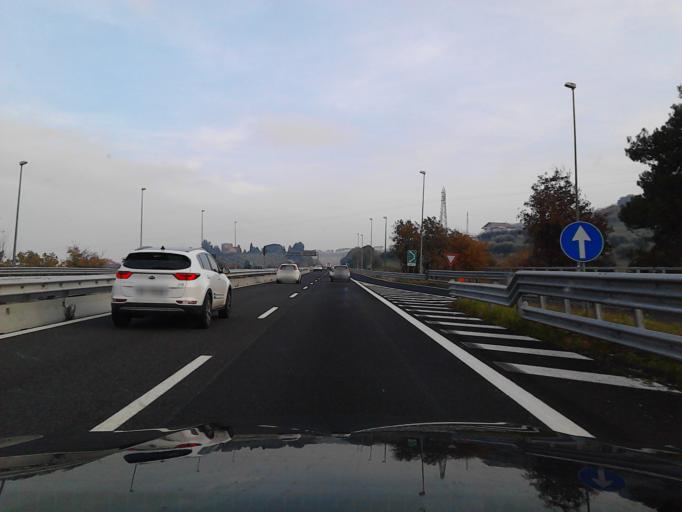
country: IT
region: Abruzzo
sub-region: Provincia di Teramo
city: Borgo Santa Maria Immacolata
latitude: 42.6062
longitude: 14.0487
